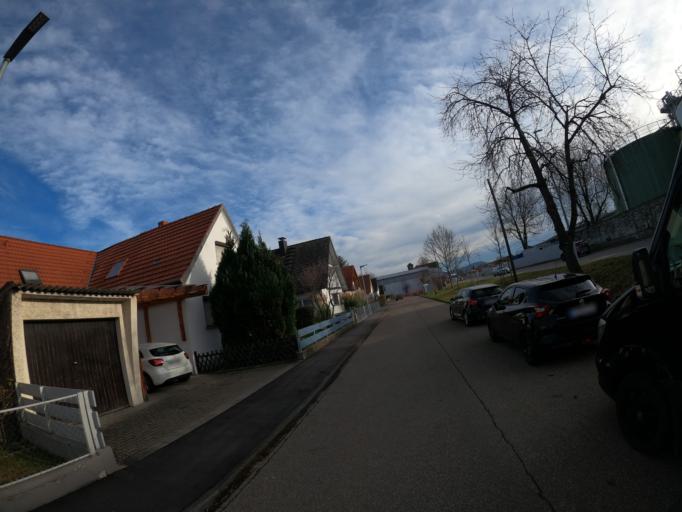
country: DE
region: Baden-Wuerttemberg
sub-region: Regierungsbezirk Stuttgart
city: Eislingen
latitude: 48.6959
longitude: 9.7141
